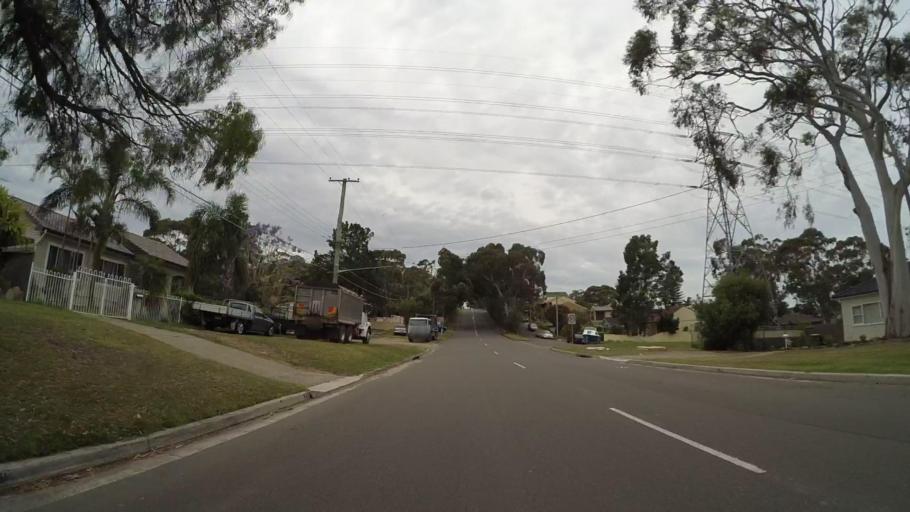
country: AU
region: New South Wales
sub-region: Sutherland Shire
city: Kareela
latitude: -34.0235
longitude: 151.0945
